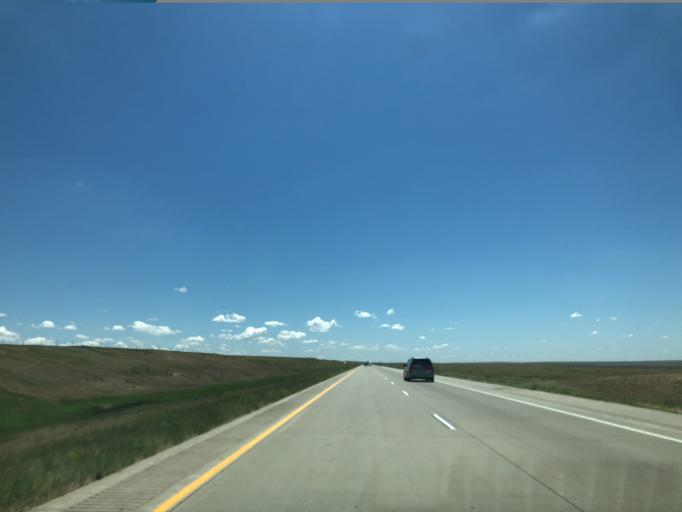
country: US
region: Colorado
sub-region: Lincoln County
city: Limon
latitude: 39.3918
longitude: -103.8944
